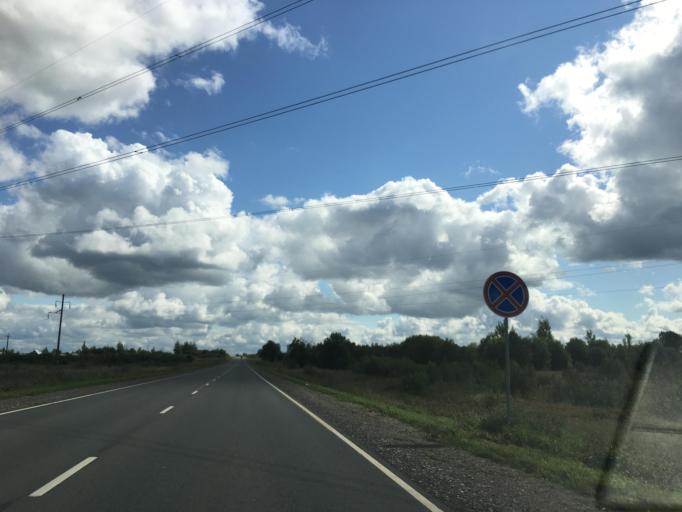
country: RU
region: Pskov
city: Pskov
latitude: 57.8286
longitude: 28.1299
